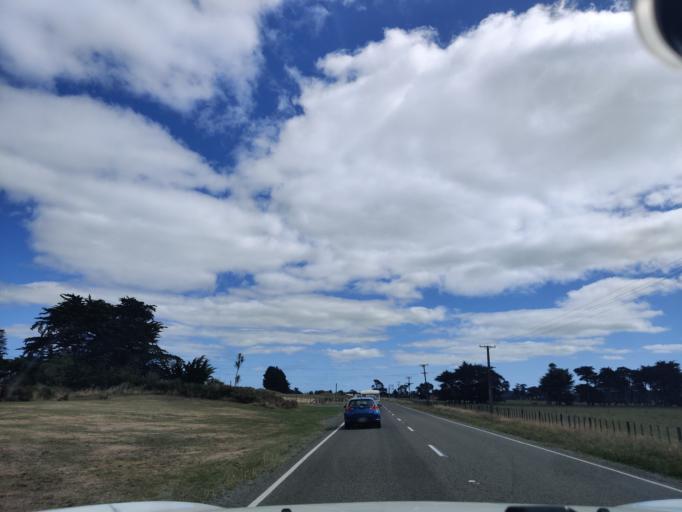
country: NZ
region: Manawatu-Wanganui
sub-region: Horowhenua District
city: Foxton
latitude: -40.4189
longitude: 175.4096
